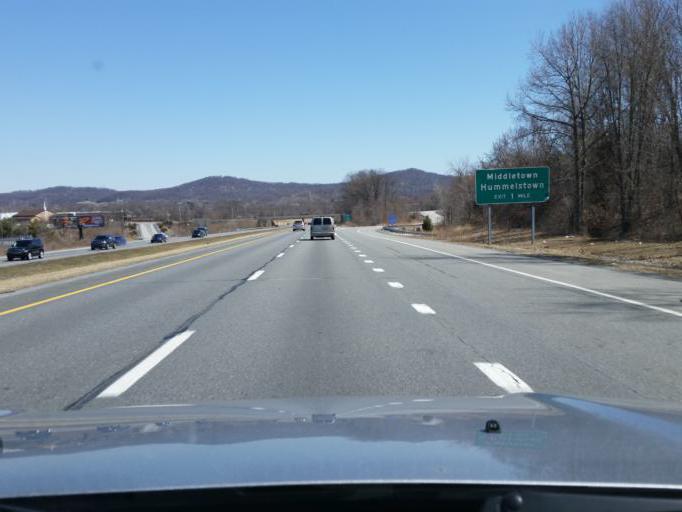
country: US
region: Pennsylvania
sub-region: Dauphin County
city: Middletown
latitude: 40.2263
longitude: -76.7445
